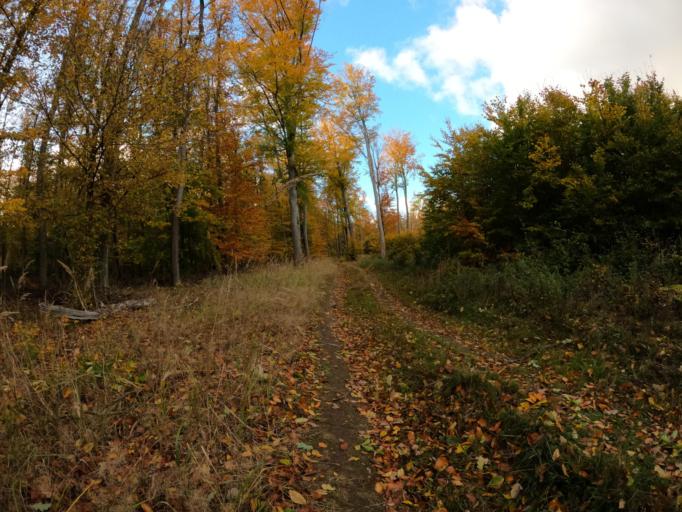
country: PL
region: West Pomeranian Voivodeship
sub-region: Powiat mysliborski
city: Barlinek
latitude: 52.9494
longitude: 15.2696
